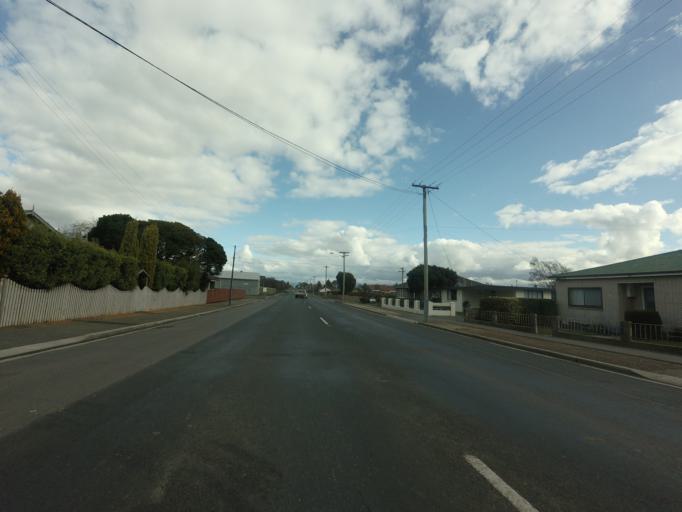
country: AU
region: Tasmania
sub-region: Northern Midlands
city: Longford
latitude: -41.6033
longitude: 147.1193
